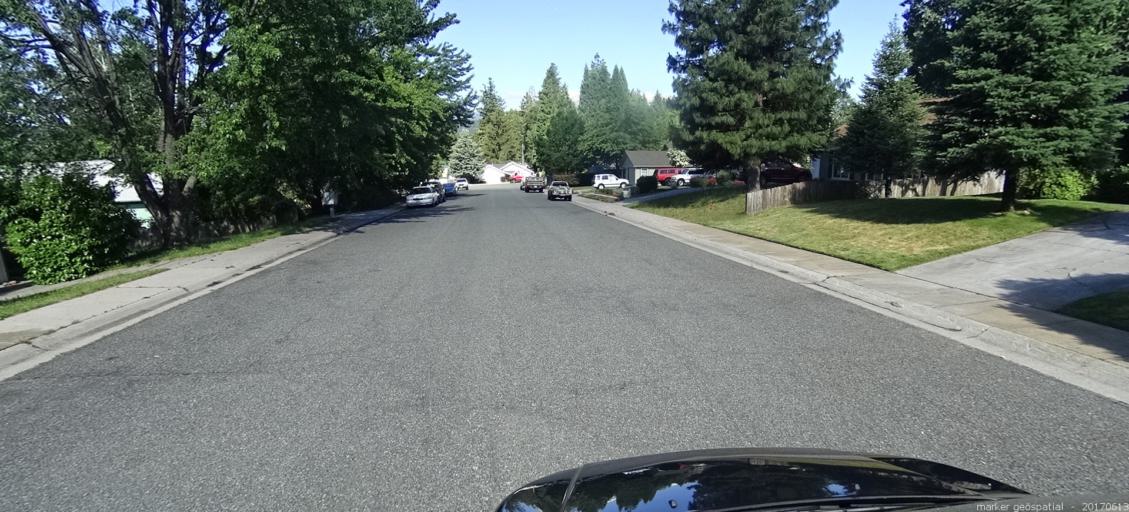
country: US
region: California
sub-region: Siskiyou County
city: Mount Shasta
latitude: 41.3038
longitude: -122.3045
